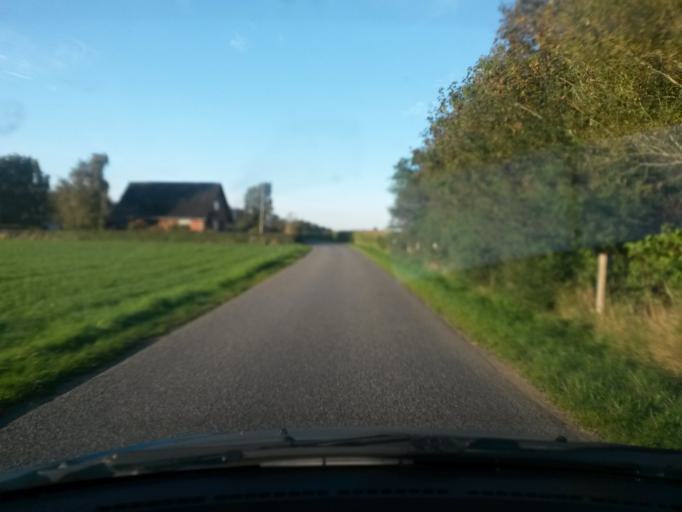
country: DK
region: Central Jutland
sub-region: Silkeborg Kommune
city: Kjellerup
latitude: 56.3300
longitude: 9.4419
